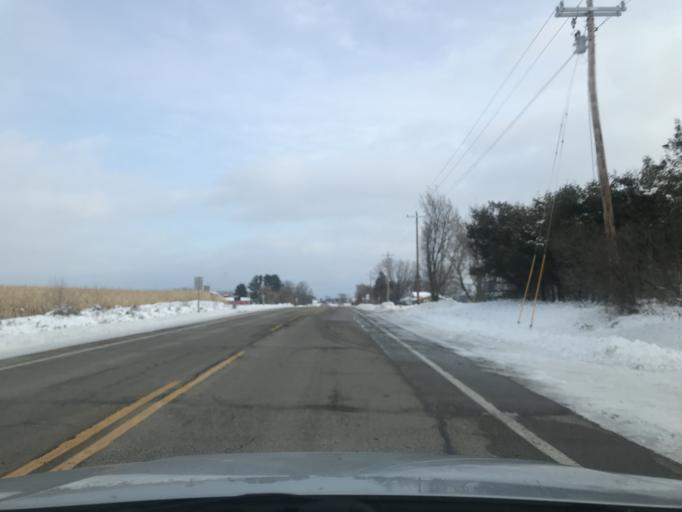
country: US
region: Wisconsin
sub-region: Oconto County
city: Oconto
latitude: 44.8929
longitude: -87.9704
